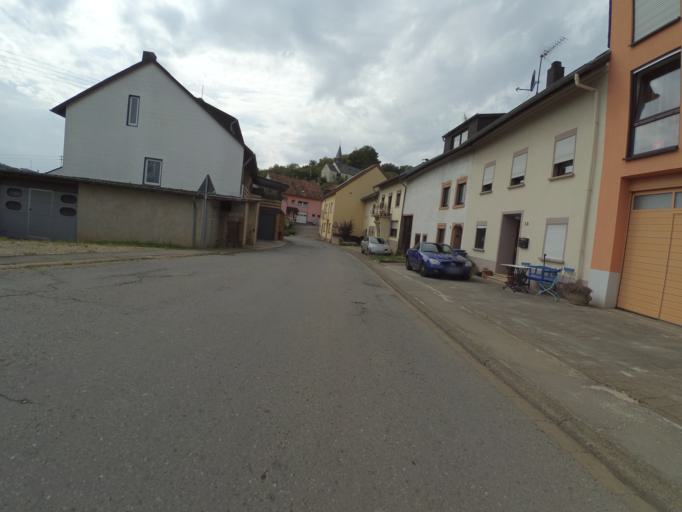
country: DE
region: Rheinland-Pfalz
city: Onsdorf
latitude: 49.6448
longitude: 6.4816
